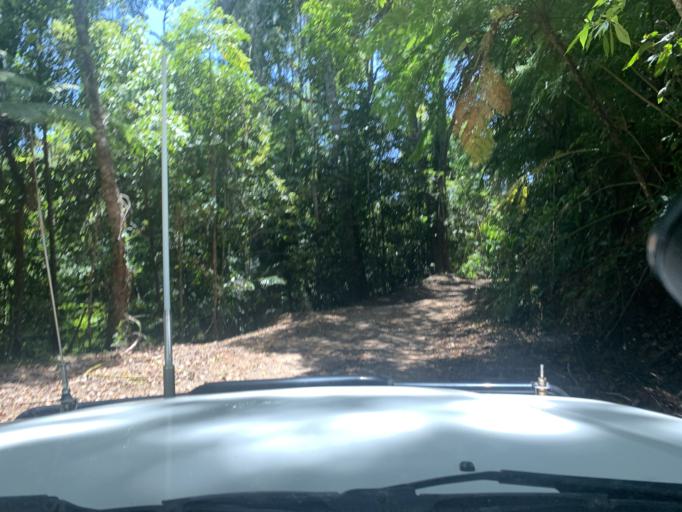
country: AU
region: Queensland
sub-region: Cairns
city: Redlynch
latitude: -16.9722
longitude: 145.6503
